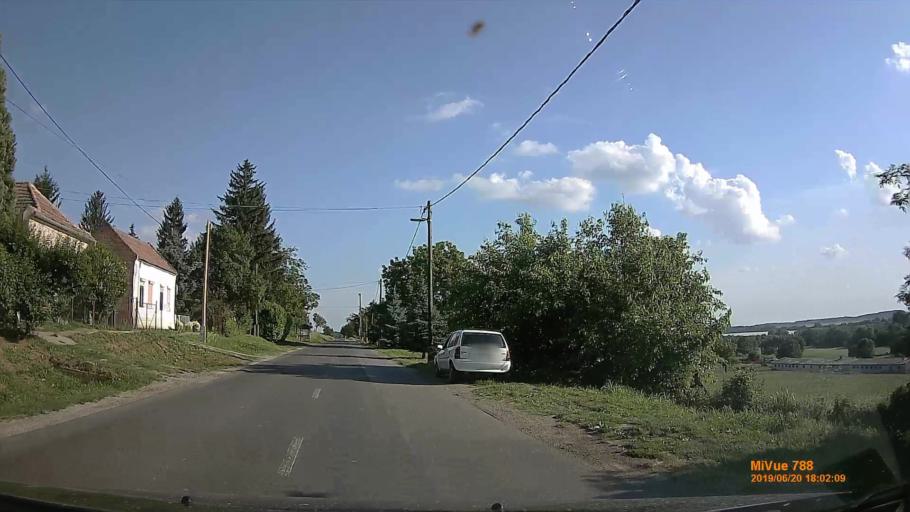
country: HU
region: Baranya
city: Buekkoesd
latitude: 46.0772
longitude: 17.9906
